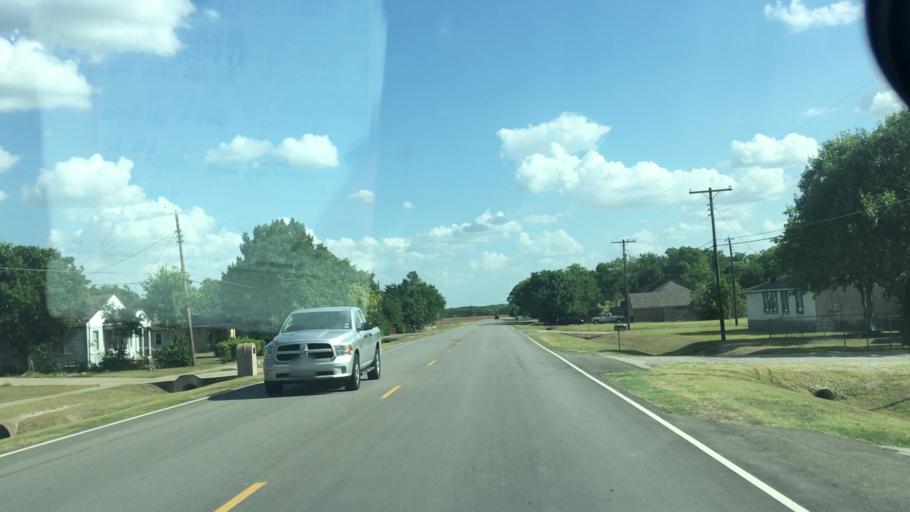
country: US
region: Texas
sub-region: Dallas County
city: Lancaster
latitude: 32.5973
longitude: -96.7479
